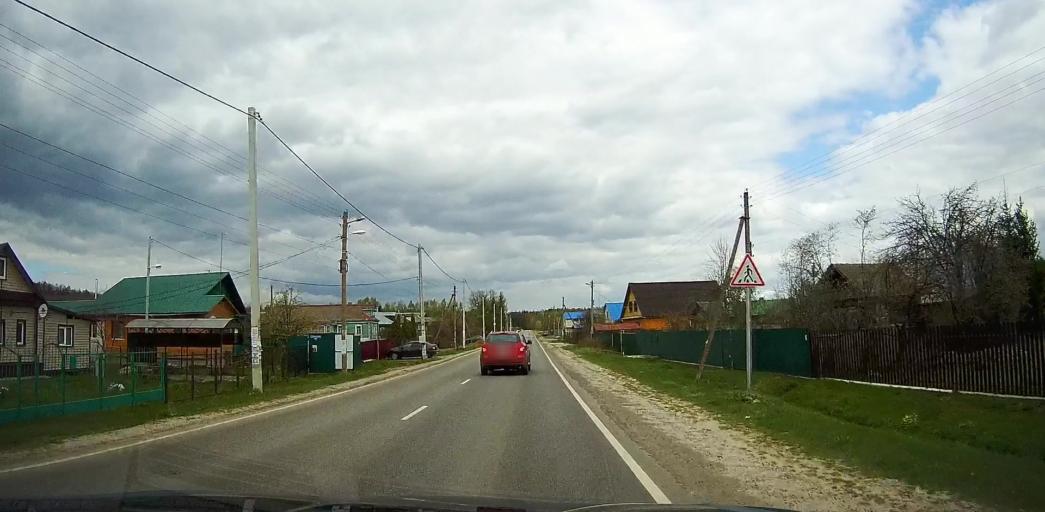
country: RU
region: Moskovskaya
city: Ashitkovo
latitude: 55.4637
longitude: 38.6057
